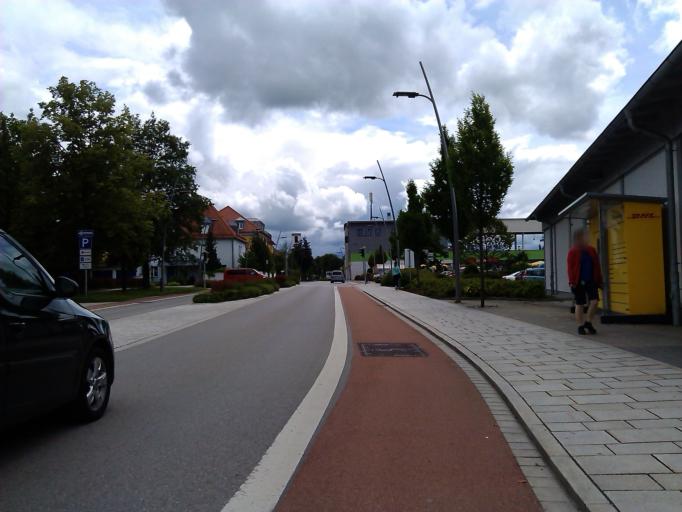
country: DE
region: Bavaria
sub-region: Swabia
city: Marktoberdorf
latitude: 47.7777
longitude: 10.6145
